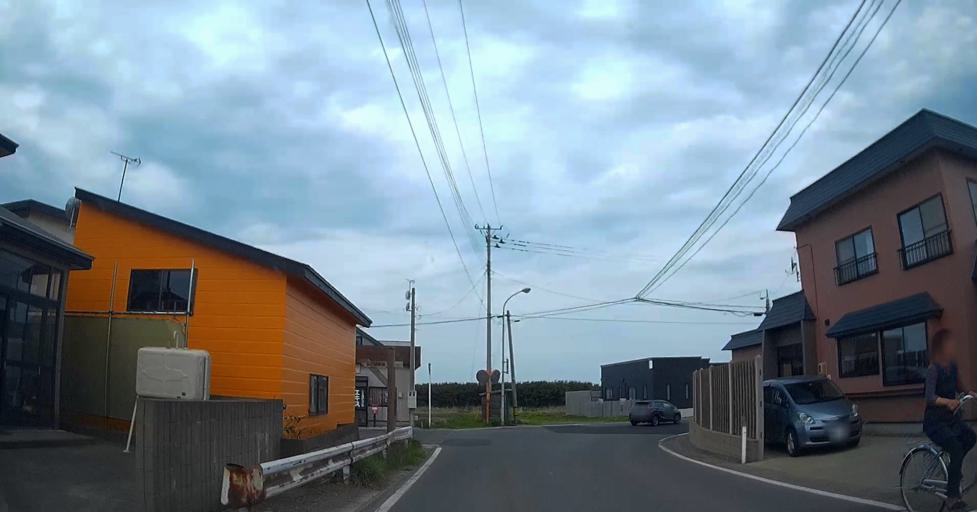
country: JP
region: Aomori
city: Shimokizukuri
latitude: 41.0260
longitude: 140.3263
